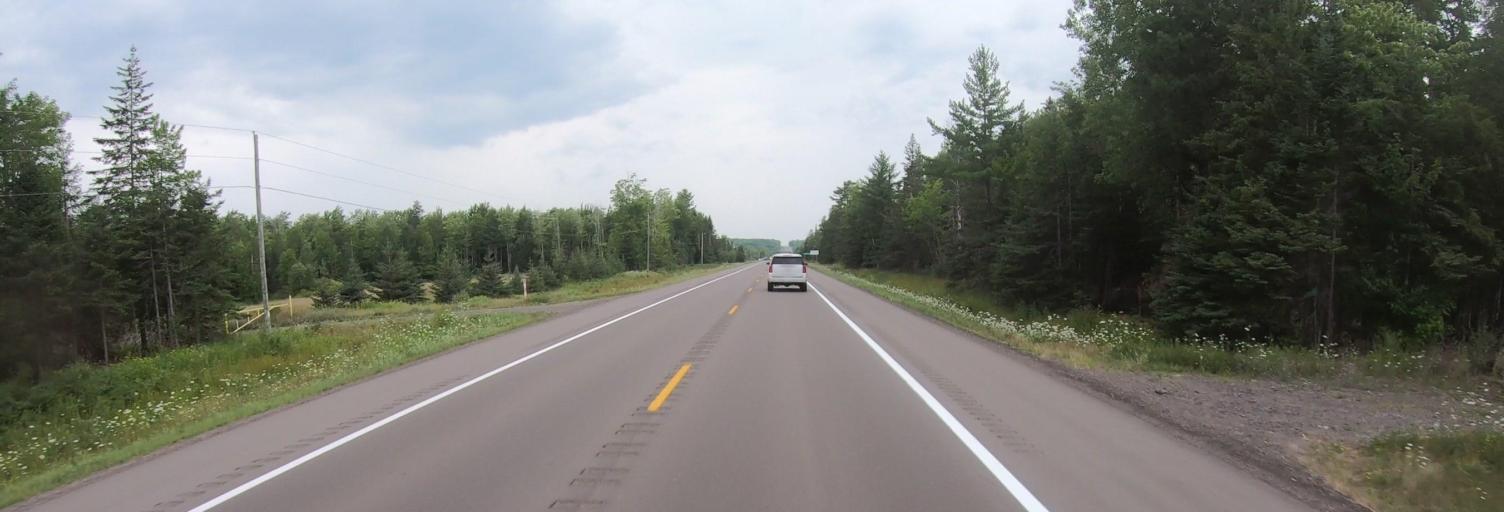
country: US
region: Michigan
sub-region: Houghton County
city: Dollar Bay
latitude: 46.9571
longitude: -88.4549
